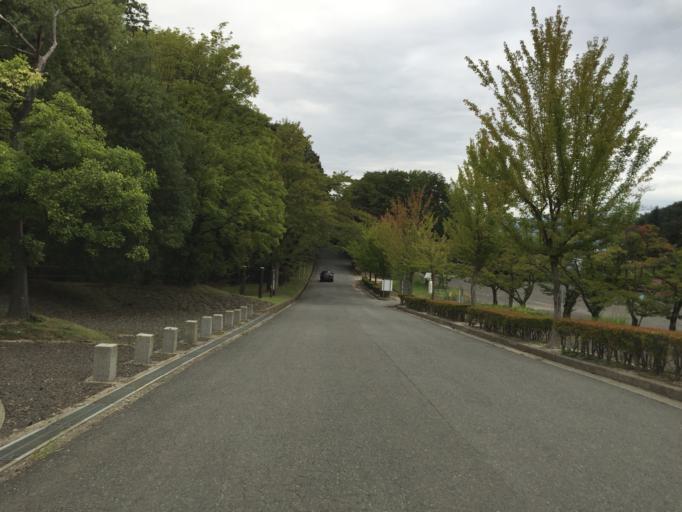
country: JP
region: Fukushima
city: Fukushima-shi
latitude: 37.7649
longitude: 140.4963
